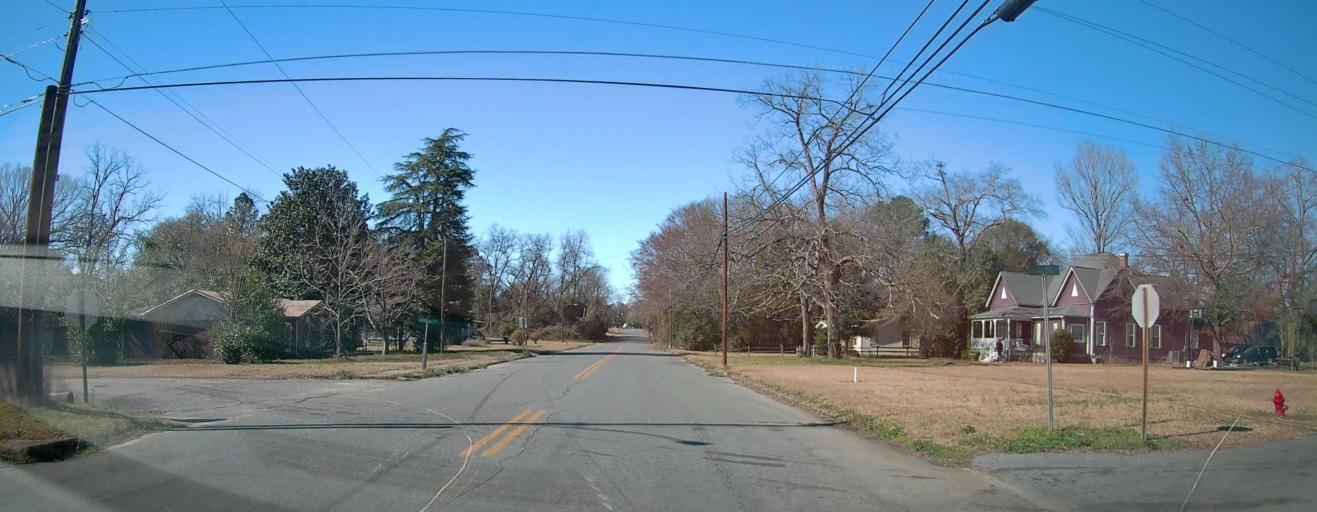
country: US
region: Georgia
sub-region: Macon County
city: Oglethorpe
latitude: 32.2962
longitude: -84.0612
